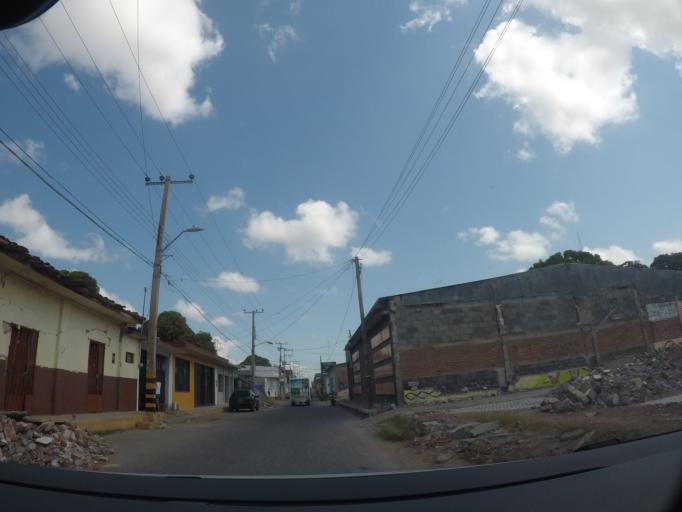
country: MX
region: Oaxaca
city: Juchitan de Zaragoza
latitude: 16.4376
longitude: -95.0210
